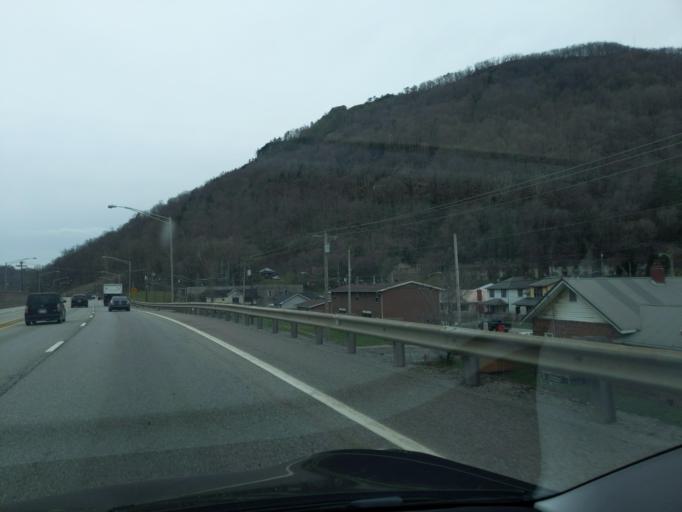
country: US
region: Kentucky
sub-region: Bell County
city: Pineville
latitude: 36.7600
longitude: -83.6936
